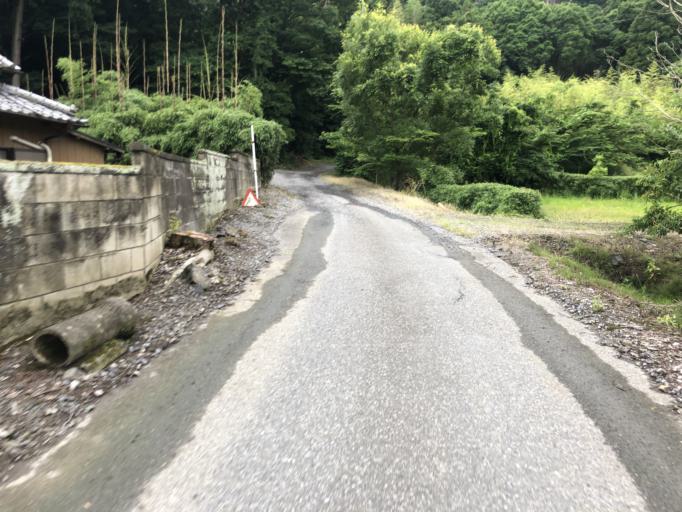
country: JP
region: Tochigi
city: Sano
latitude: 36.3331
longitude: 139.6585
